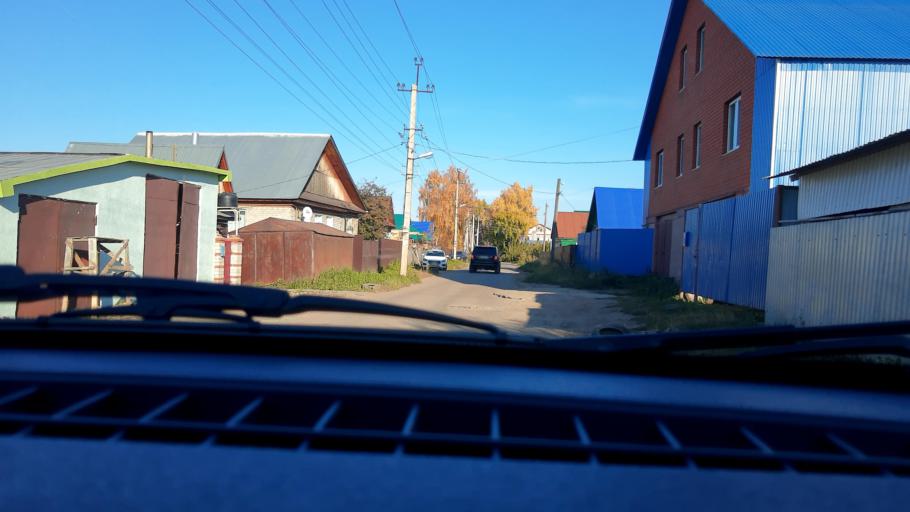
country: RU
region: Bashkortostan
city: Mikhaylovka
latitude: 54.7631
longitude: 55.9106
